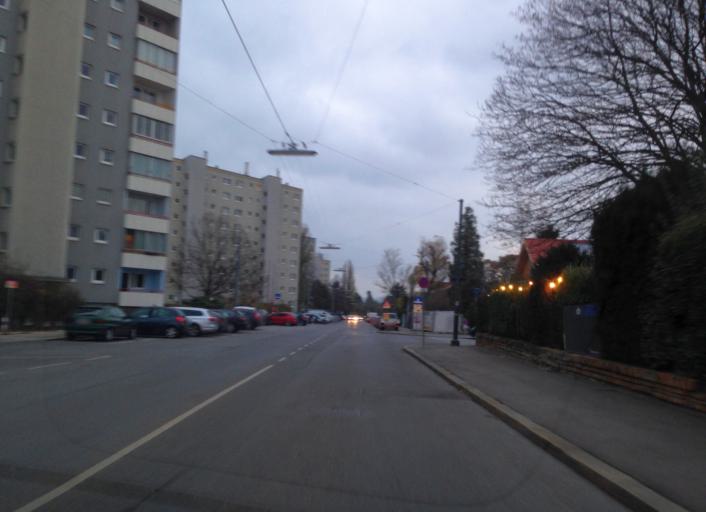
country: AT
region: Lower Austria
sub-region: Politischer Bezirk Korneuburg
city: Langenzersdorf
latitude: 48.2778
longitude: 16.3875
